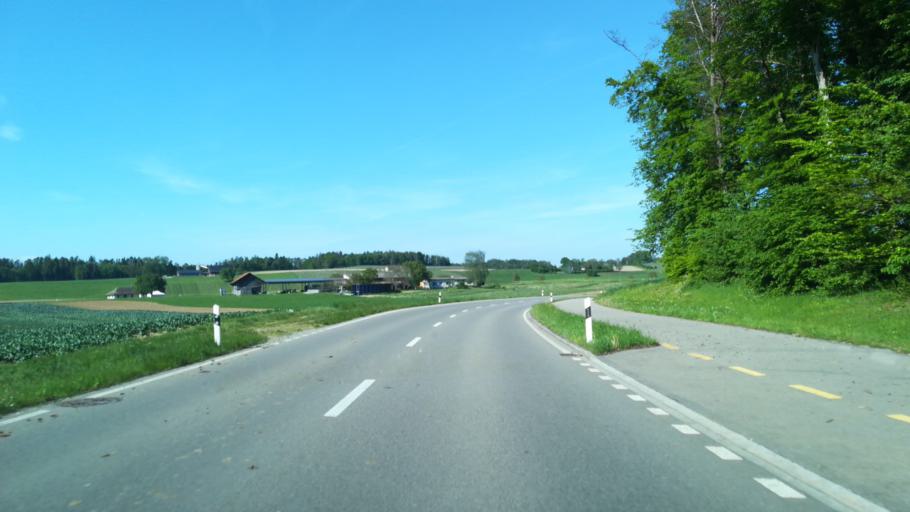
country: CH
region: Zurich
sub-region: Bezirk Andelfingen
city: Kleinandelfingen
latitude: 47.6082
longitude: 8.7061
